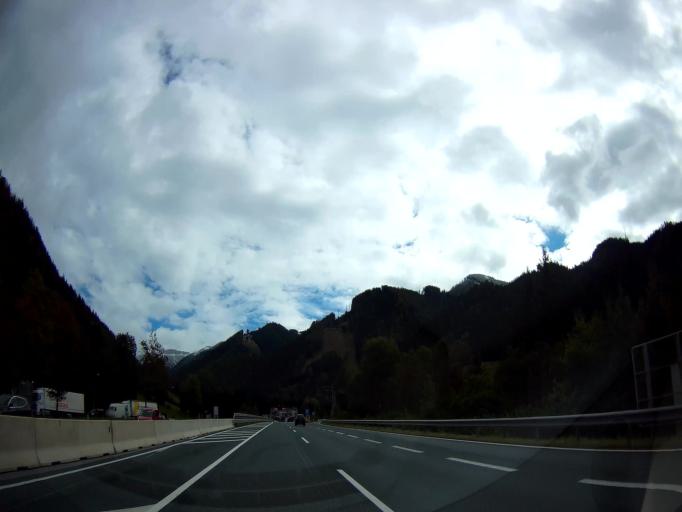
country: AT
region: Styria
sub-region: Politischer Bezirk Leoben
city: Sankt Michael in Obersteiermark
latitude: 47.2986
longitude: 15.0704
